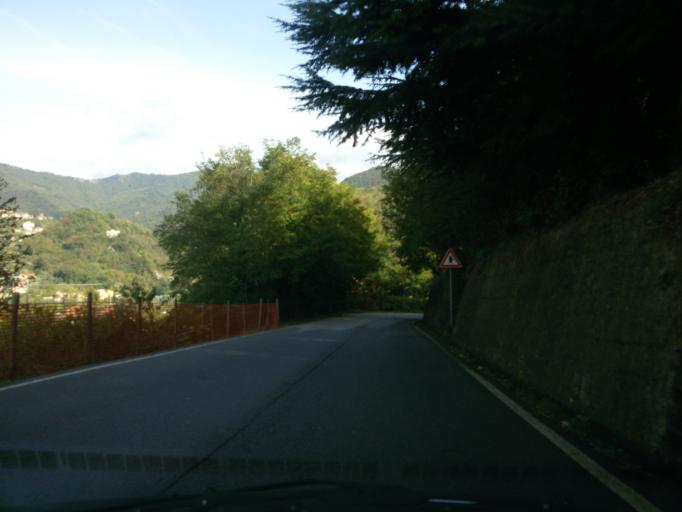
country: IT
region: Liguria
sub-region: Provincia di Genova
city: Piccarello
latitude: 44.4802
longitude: 8.9643
